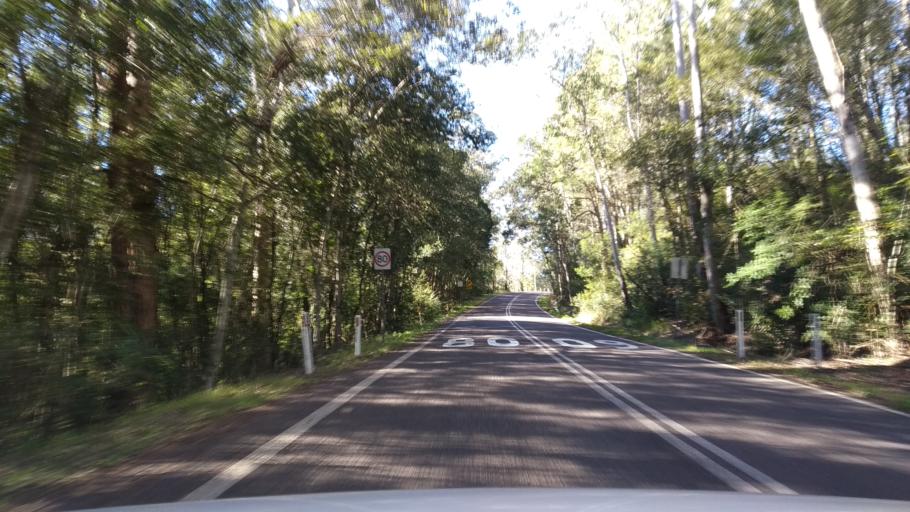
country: AU
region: New South Wales
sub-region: Wyong Shire
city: Little Jilliby
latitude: -33.2284
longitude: 151.2937
